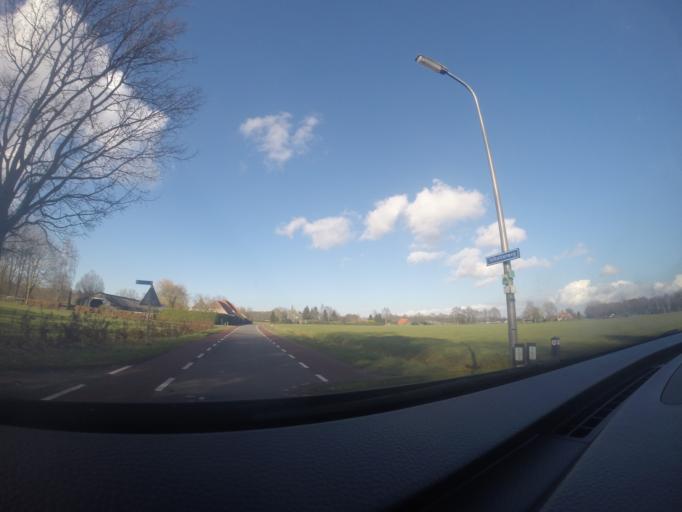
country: NL
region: Gelderland
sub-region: Gemeente Lochem
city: Barchem
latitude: 52.0691
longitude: 6.4493
